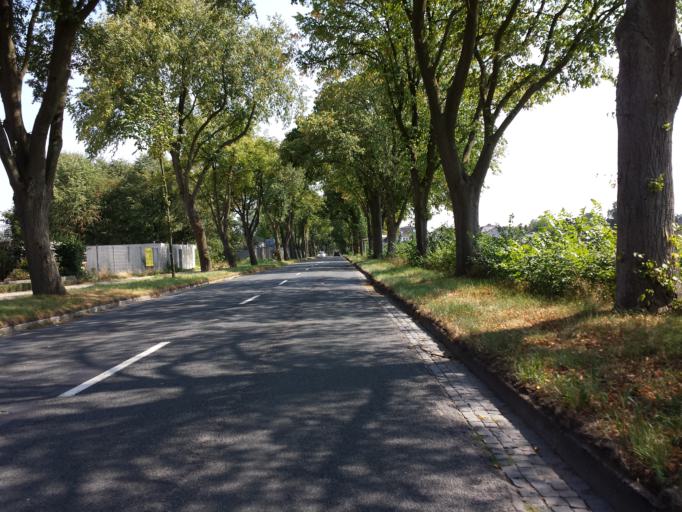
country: DE
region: Bremen
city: Bremen
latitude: 53.0256
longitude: 8.8552
